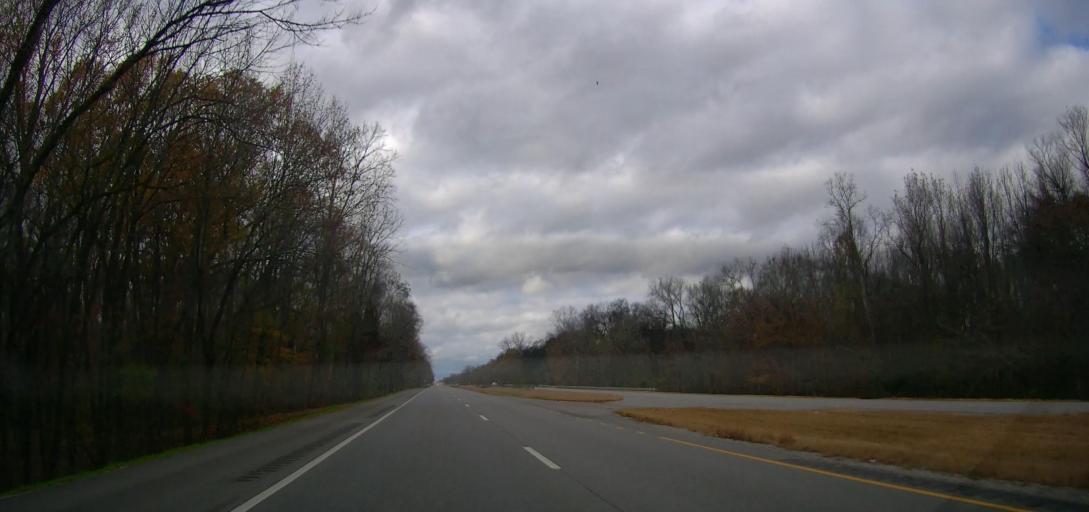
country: US
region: Alabama
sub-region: Lawrence County
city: Town Creek
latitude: 34.6304
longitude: -87.4843
